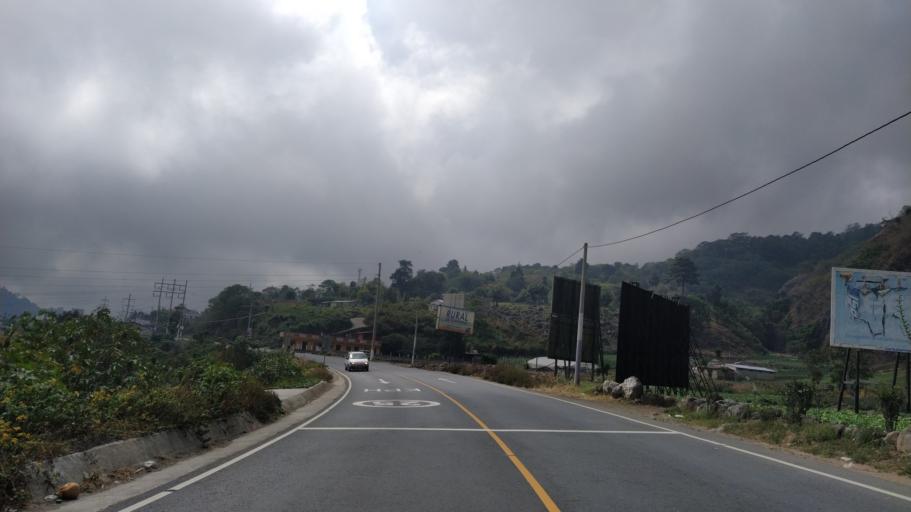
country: GT
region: Quetzaltenango
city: Zunil
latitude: 14.7528
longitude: -91.5090
